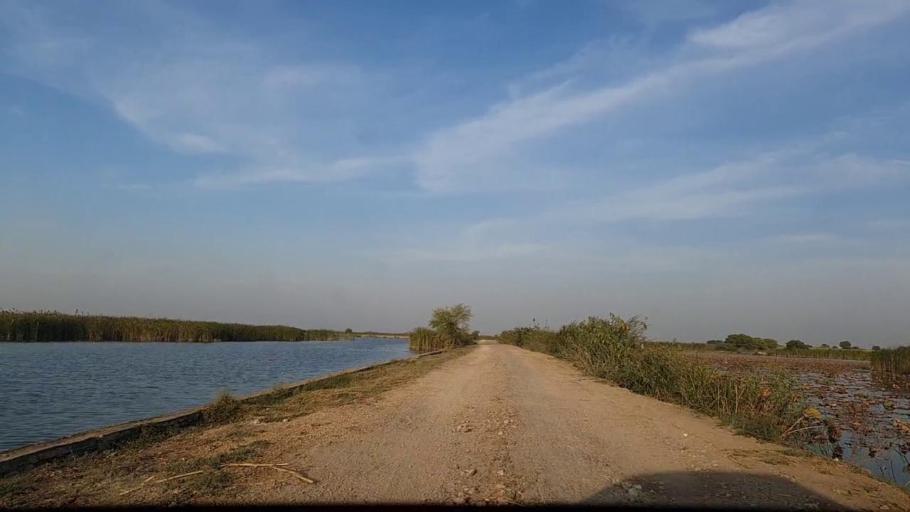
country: PK
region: Sindh
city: Mirpur Batoro
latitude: 24.6530
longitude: 68.1448
